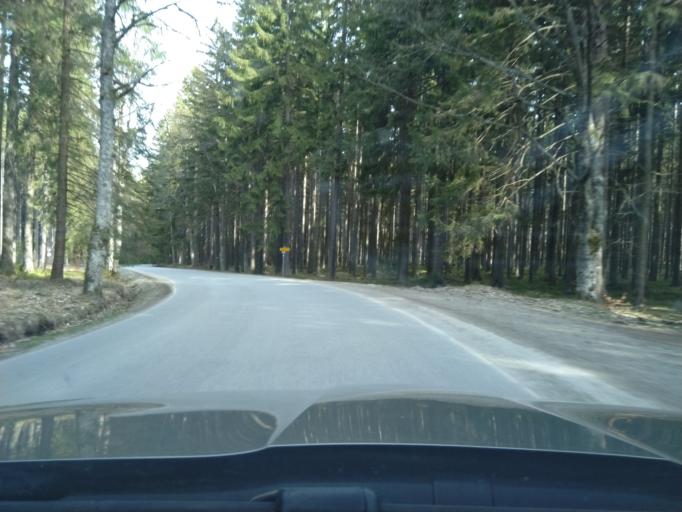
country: CZ
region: Jihocesky
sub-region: Okres Prachatice
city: Stachy
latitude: 49.0659
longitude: 13.6510
